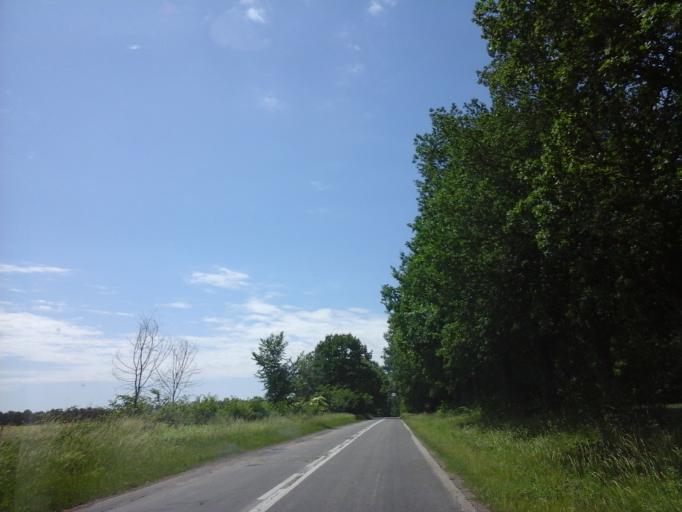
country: PL
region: West Pomeranian Voivodeship
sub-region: Powiat stargardzki
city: Dolice
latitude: 53.2071
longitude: 15.2820
